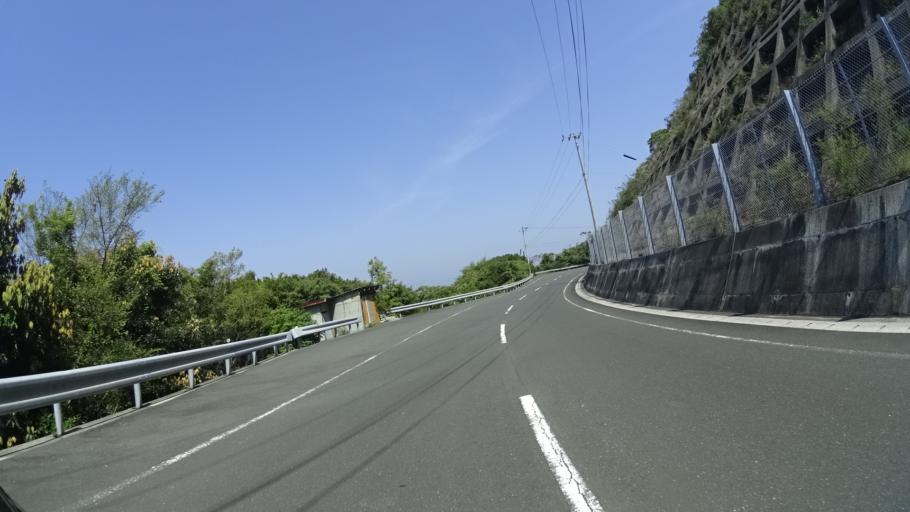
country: JP
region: Oita
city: Tsukumiura
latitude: 33.3614
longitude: 132.0392
